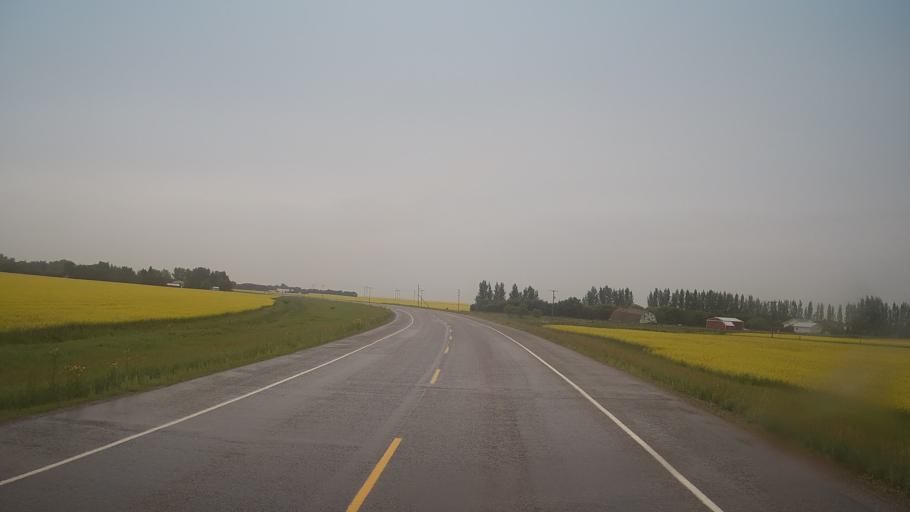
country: CA
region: Saskatchewan
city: Wilkie
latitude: 52.2005
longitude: -108.4396
